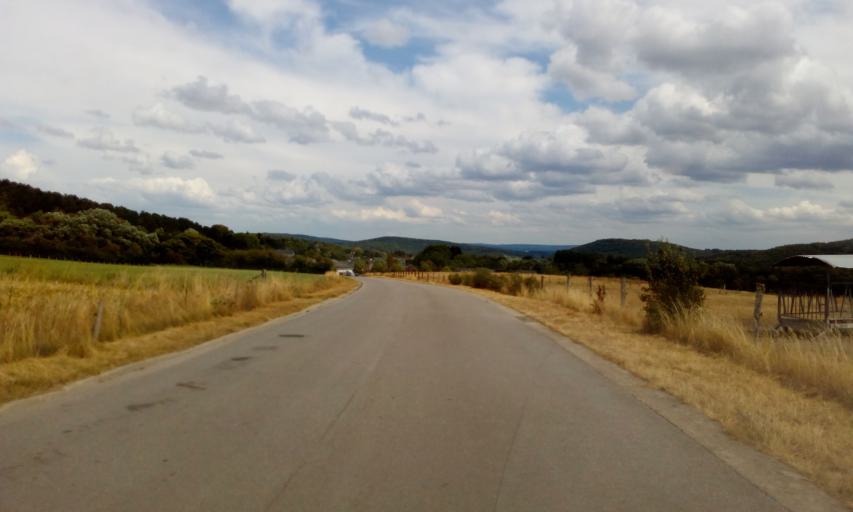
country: BE
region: Wallonia
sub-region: Province du Luxembourg
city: Wellin
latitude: 50.1068
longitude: 5.1298
